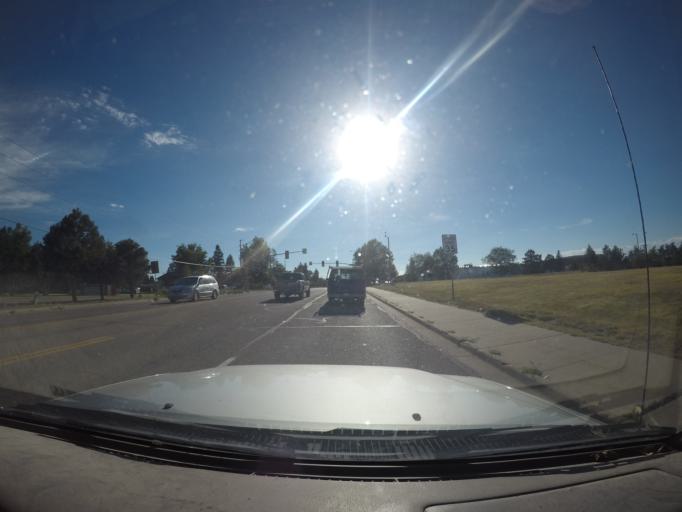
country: US
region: Wyoming
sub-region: Laramie County
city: Fox Farm-College
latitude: 41.1457
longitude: -104.7746
